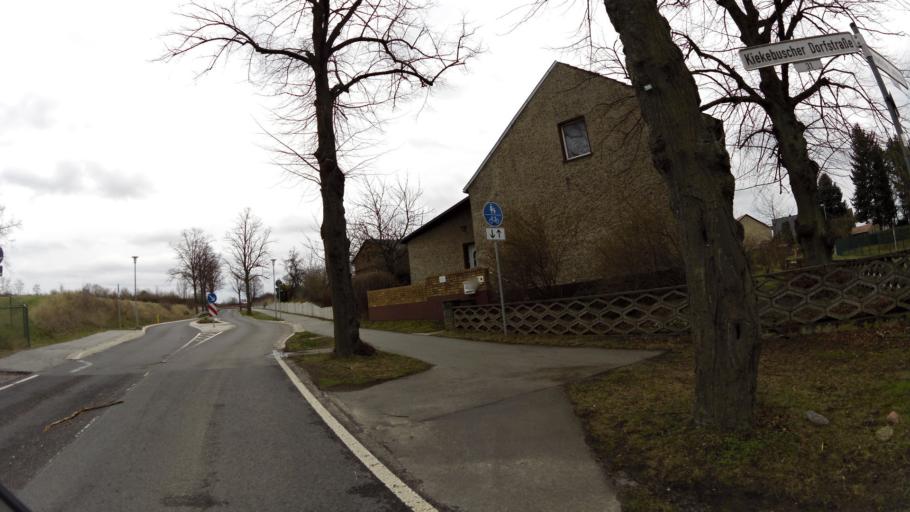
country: DE
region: Brandenburg
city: Schulzendorf
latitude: 52.3449
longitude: 13.5526
